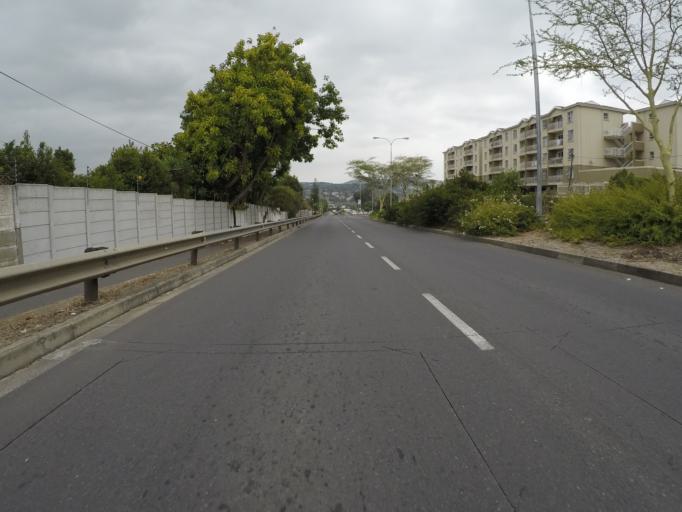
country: ZA
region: Western Cape
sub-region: City of Cape Town
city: Kraaifontein
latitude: -33.8726
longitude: 18.6417
